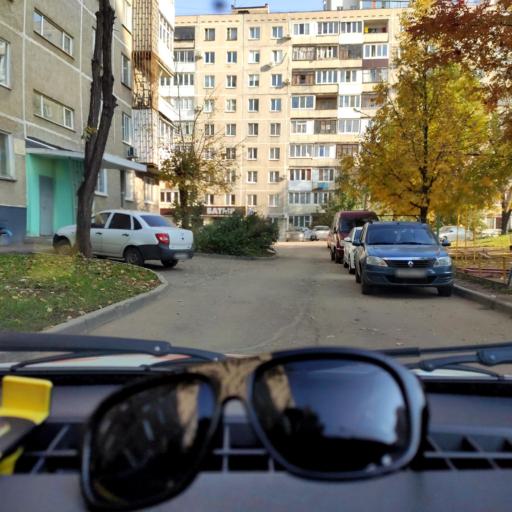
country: RU
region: Bashkortostan
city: Ufa
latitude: 54.7122
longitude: 55.9759
